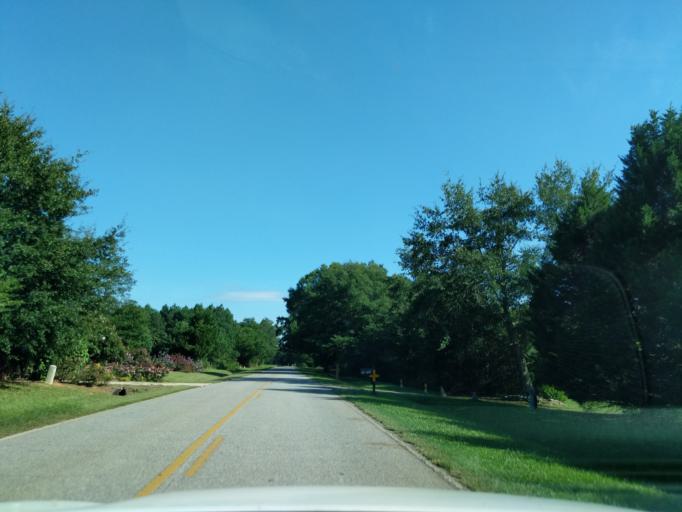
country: US
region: Georgia
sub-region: Oglethorpe County
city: Lexington
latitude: 33.9169
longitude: -83.0169
